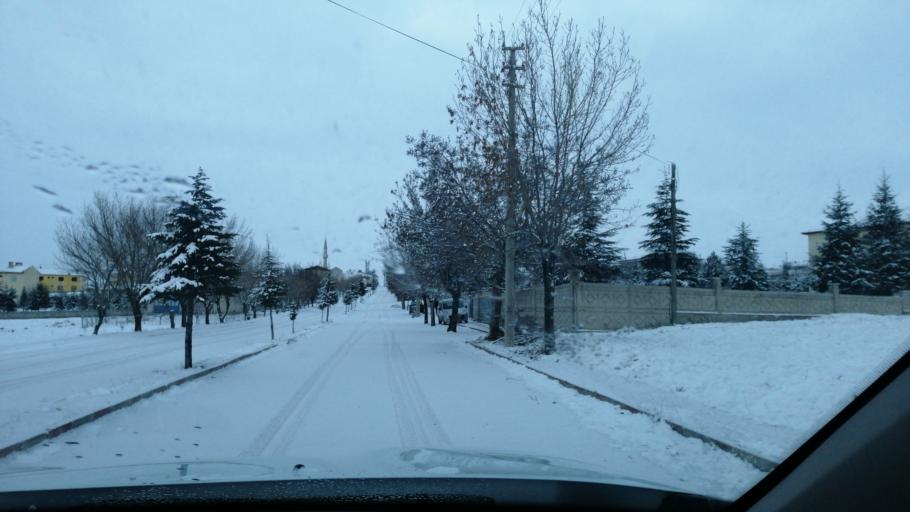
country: TR
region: Aksaray
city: Agacoren
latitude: 38.9296
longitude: 33.9536
